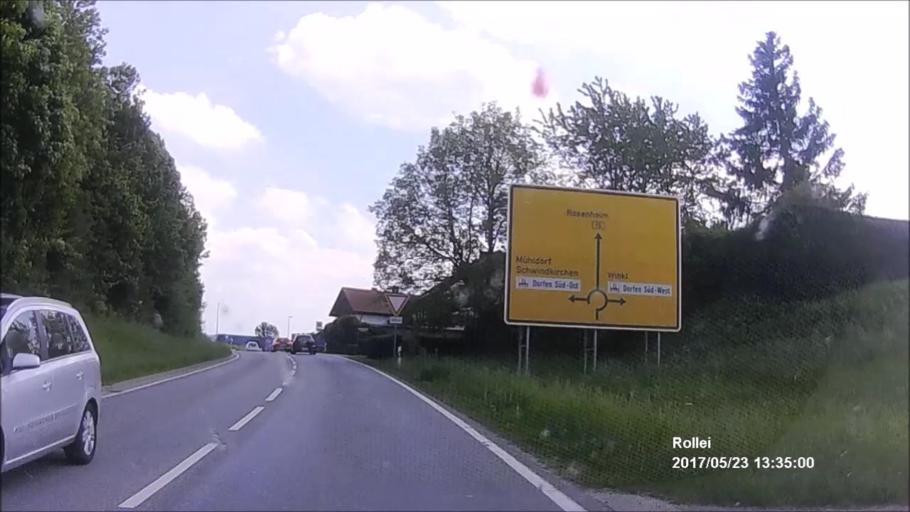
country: DE
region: Bavaria
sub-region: Upper Bavaria
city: Dorfen
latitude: 48.2615
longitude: 12.1579
